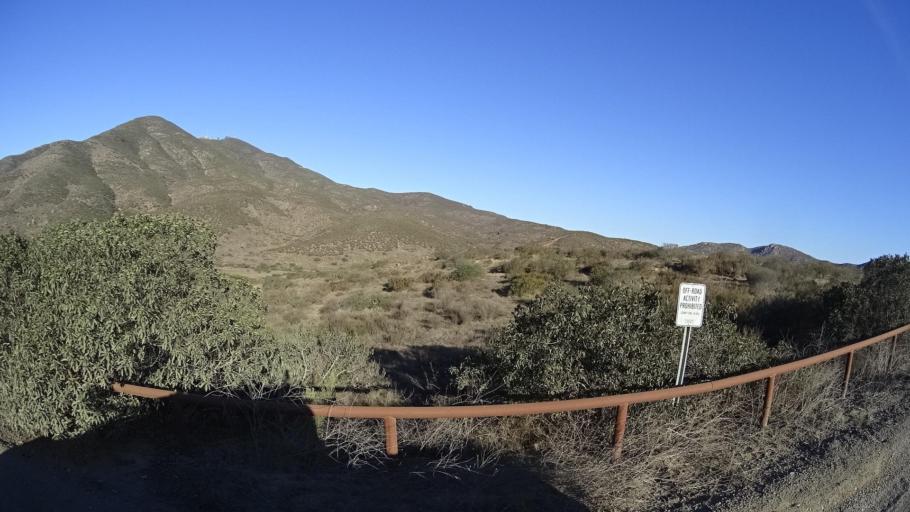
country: US
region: California
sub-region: San Diego County
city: Jamul
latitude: 32.6922
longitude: -116.9068
